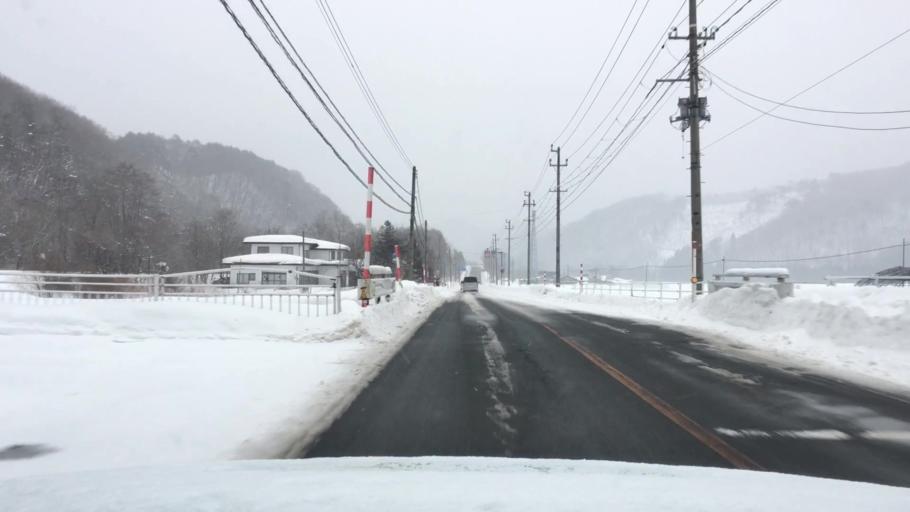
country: JP
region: Akita
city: Hanawa
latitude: 40.0579
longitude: 141.0109
